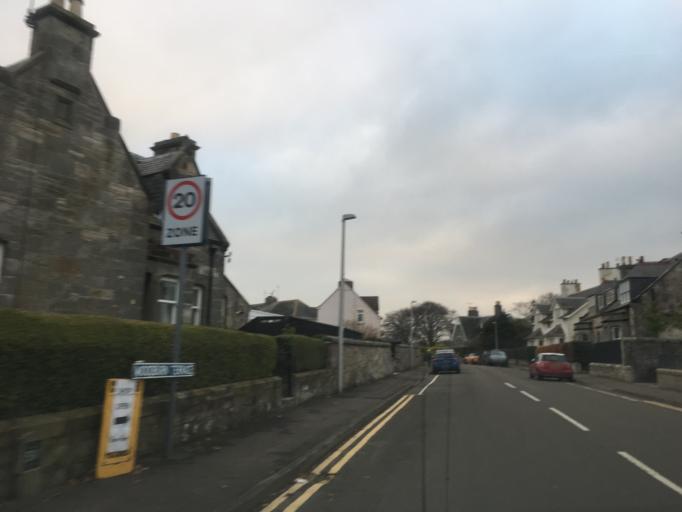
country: GB
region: Scotland
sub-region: Fife
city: Saint Andrews
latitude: 56.3357
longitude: -2.7841
